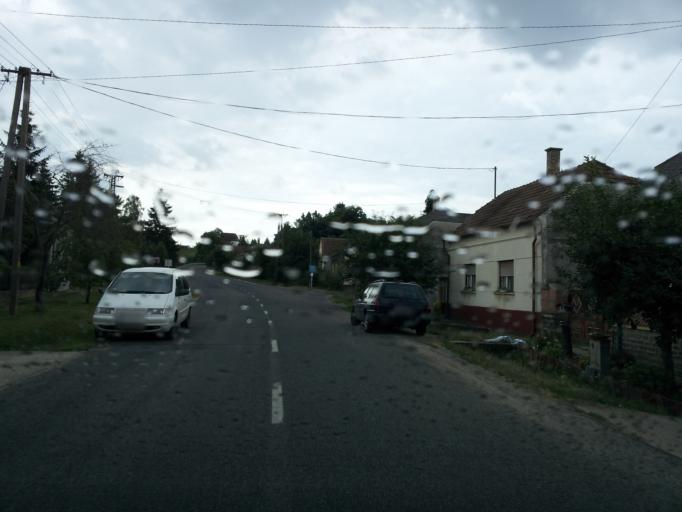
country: HU
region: Zala
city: Turje
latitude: 47.0873
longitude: 17.0231
